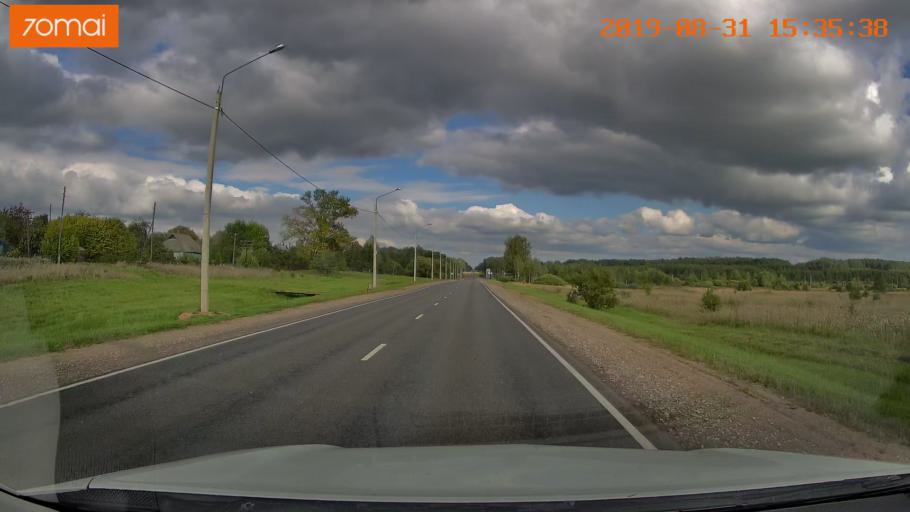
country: RU
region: Kaluga
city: Mosal'sk
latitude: 54.6065
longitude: 34.7417
